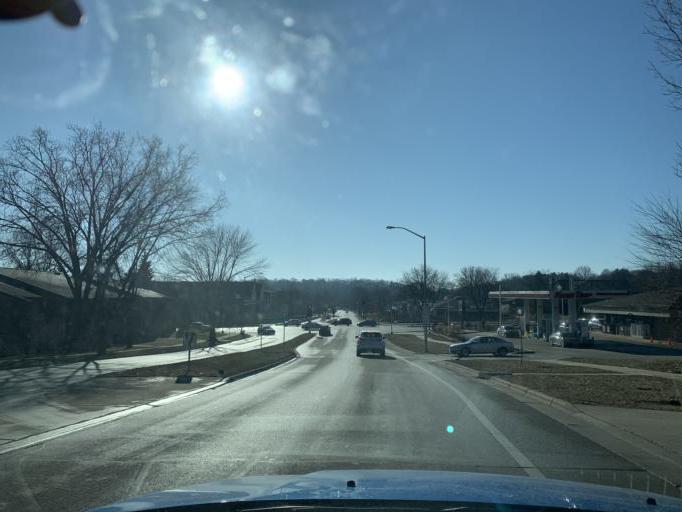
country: US
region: Wisconsin
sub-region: Dane County
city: Verona
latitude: 43.0328
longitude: -89.4970
